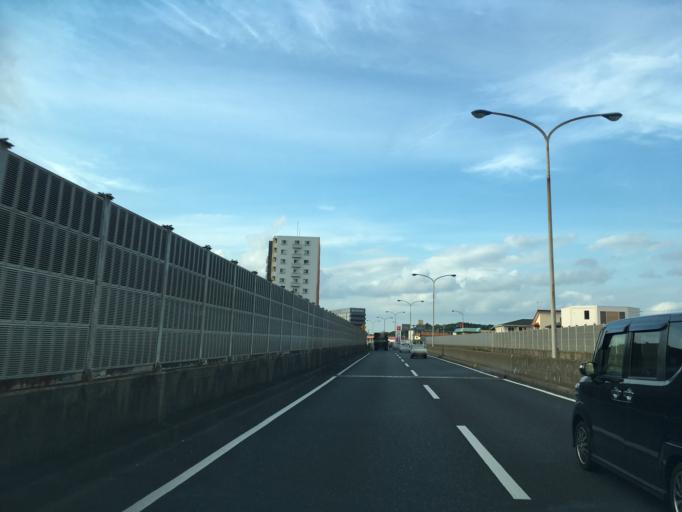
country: JP
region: Chiba
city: Kisarazu
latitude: 35.3779
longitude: 139.9418
